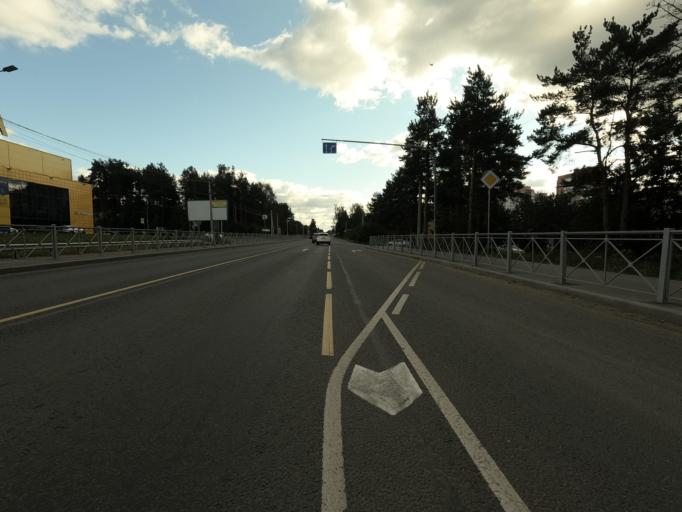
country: RU
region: Leningrad
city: Vsevolozhsk
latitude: 59.9911
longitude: 30.6579
